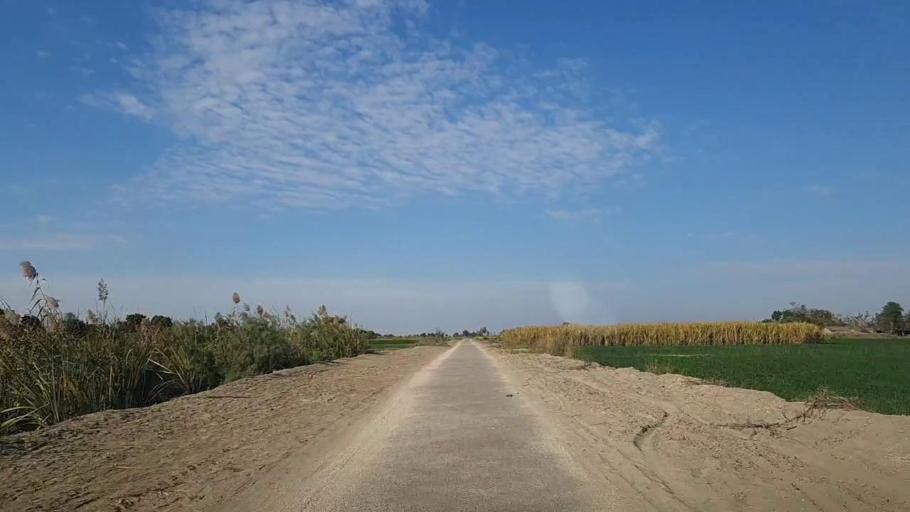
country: PK
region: Sindh
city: Khadro
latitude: 26.3034
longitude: 68.8343
